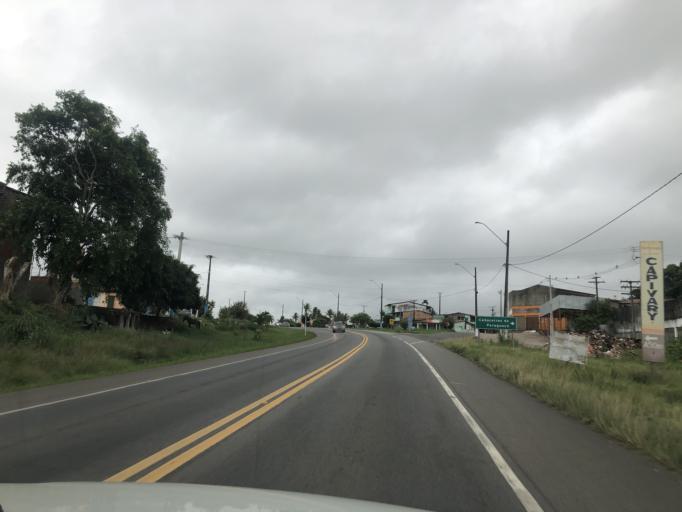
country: BR
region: Bahia
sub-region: Cruz Das Almas
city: Cruz das Almas
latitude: -12.6010
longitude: -39.0488
